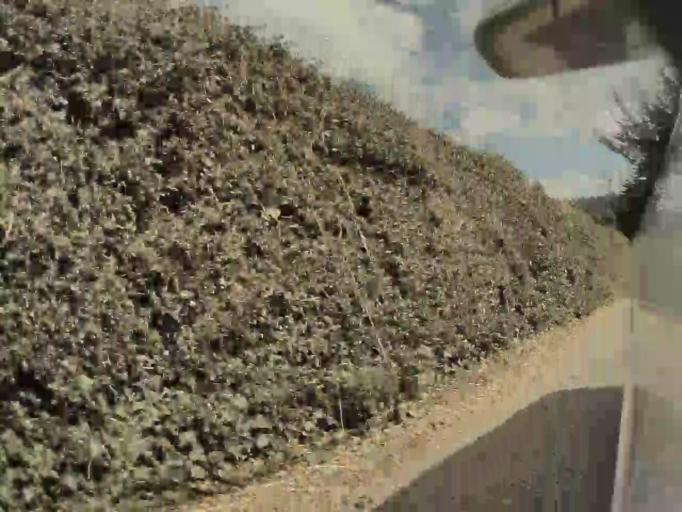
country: IE
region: Leinster
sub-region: Wicklow
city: Kilmacanoge
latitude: 53.1431
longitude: -6.1284
